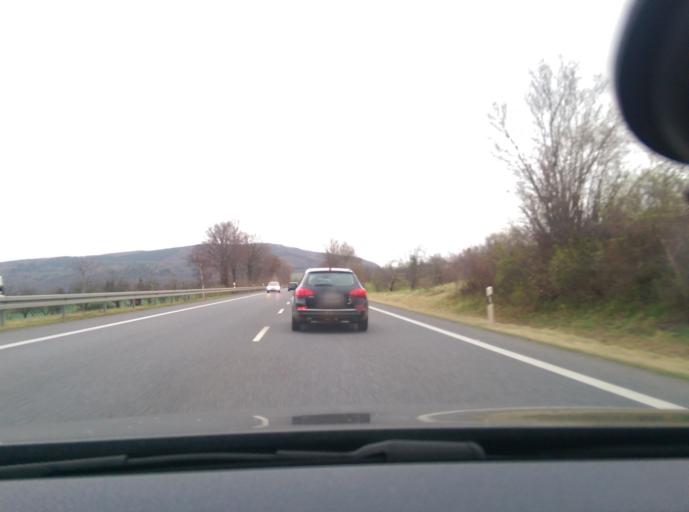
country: DE
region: Hesse
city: Witzenhausen
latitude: 51.3276
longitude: 9.8858
